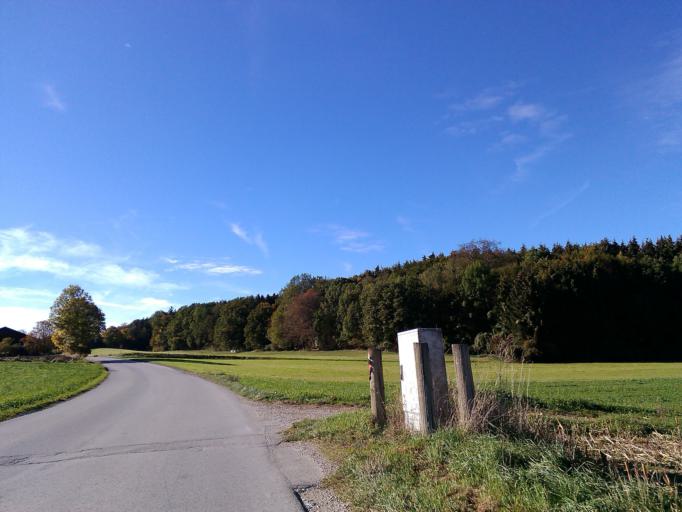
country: DE
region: Bavaria
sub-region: Upper Bavaria
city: Wessling
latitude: 48.0563
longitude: 11.2816
